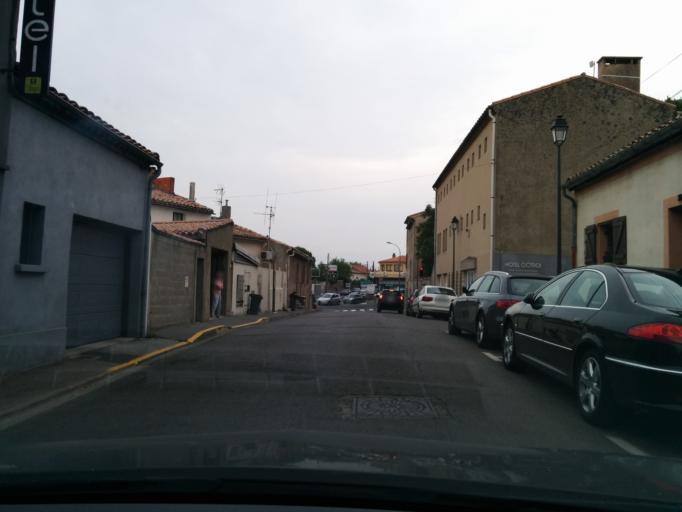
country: FR
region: Languedoc-Roussillon
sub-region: Departement de l'Aude
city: Carcassonne
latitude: 43.2086
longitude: 2.3683
